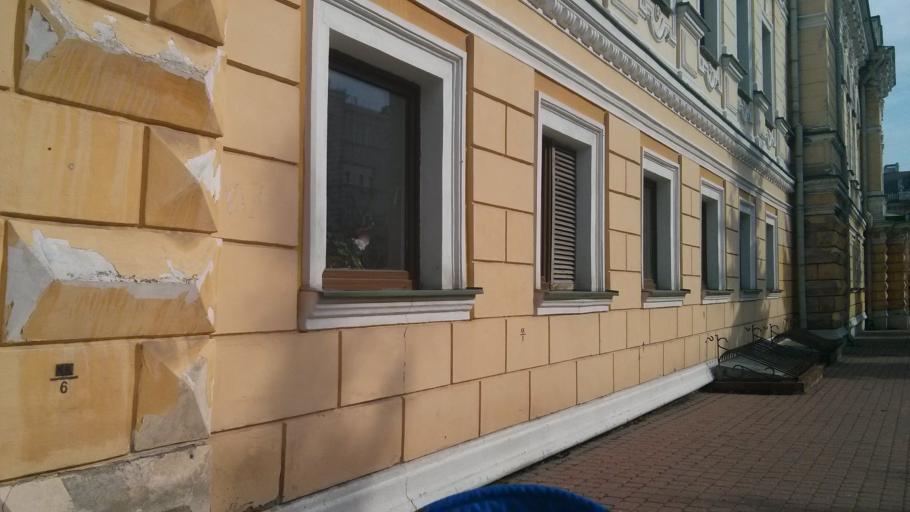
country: RU
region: Nizjnij Novgorod
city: Nizhniy Novgorod
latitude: 56.3241
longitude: 44.0007
